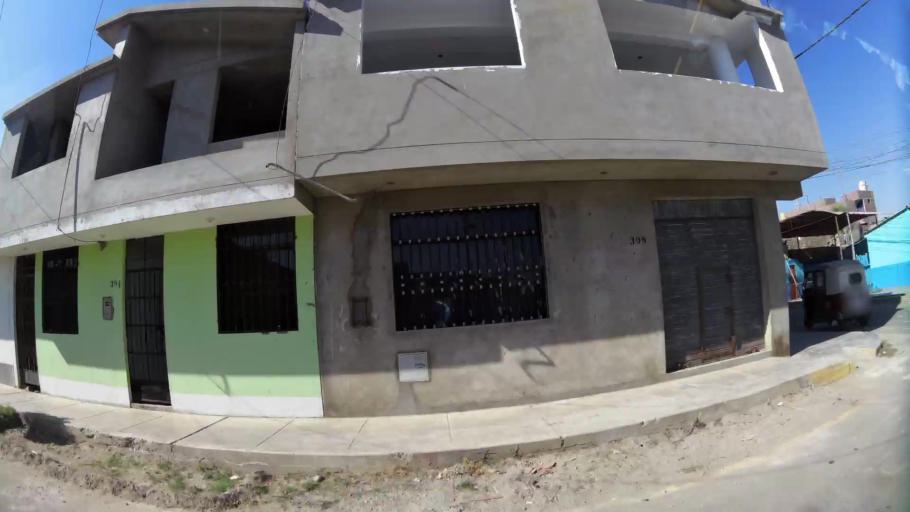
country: PE
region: Ica
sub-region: Provincia de Ica
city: La Tinguina
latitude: -14.0441
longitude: -75.7101
